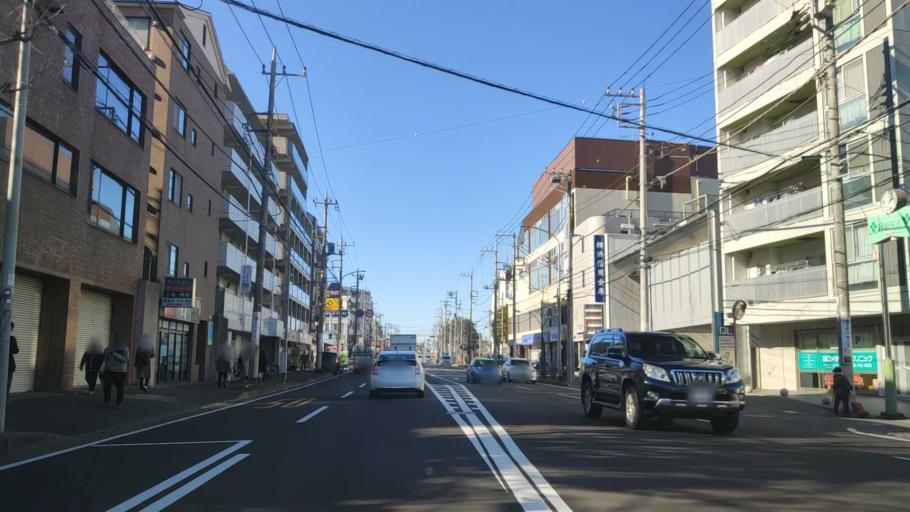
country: JP
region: Tokyo
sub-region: Machida-shi
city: Machida
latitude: 35.5146
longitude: 139.5366
